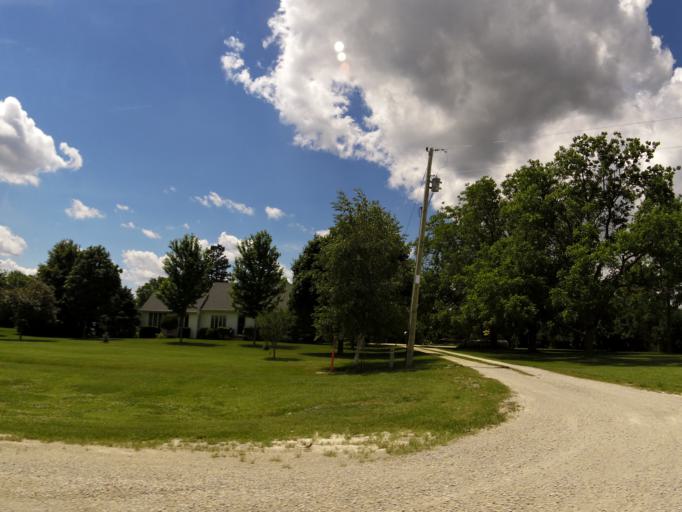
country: US
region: Iowa
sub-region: Buchanan County
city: Independence
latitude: 42.5349
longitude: -91.8900
